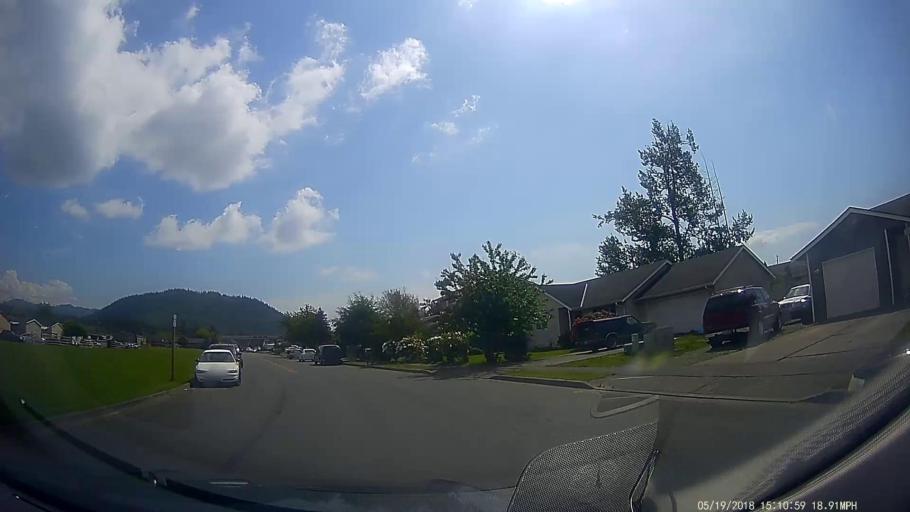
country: US
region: Washington
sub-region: Skagit County
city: Mount Vernon
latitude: 48.4161
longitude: -122.3113
